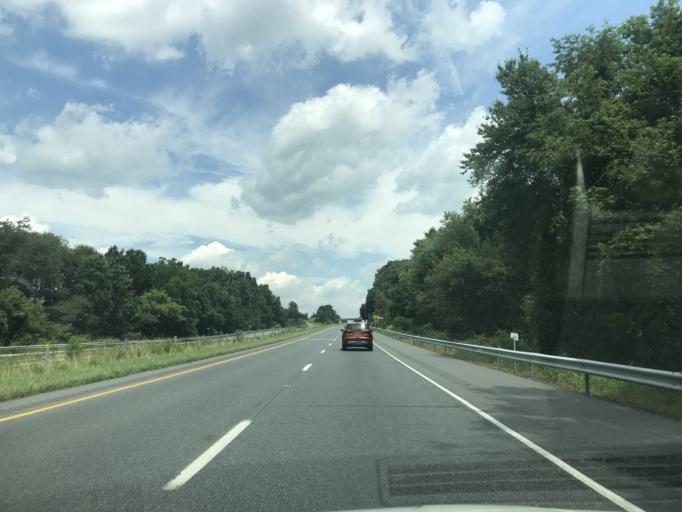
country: US
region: Pennsylvania
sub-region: Chester County
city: Oxford
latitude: 39.7827
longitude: -76.0005
